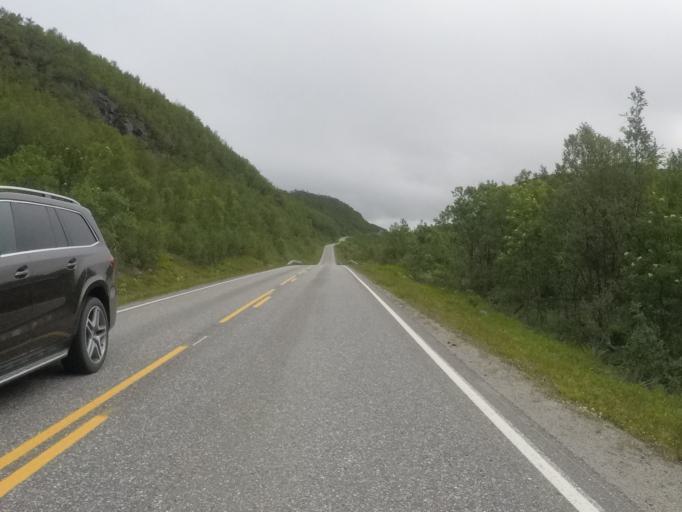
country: NO
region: Finnmark Fylke
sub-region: Alta
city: Alta
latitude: 70.1271
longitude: 23.6057
